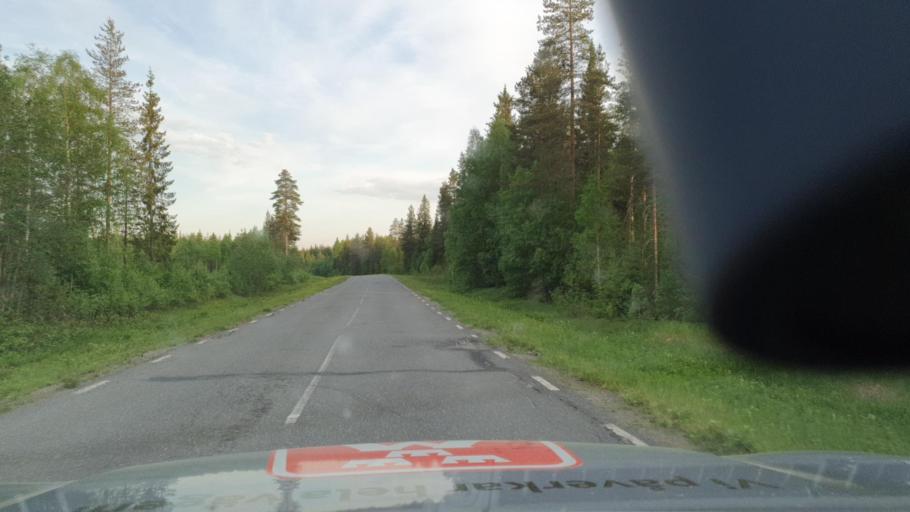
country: SE
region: Norrbotten
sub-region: Bodens Kommun
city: Boden
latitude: 66.2654
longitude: 21.3400
